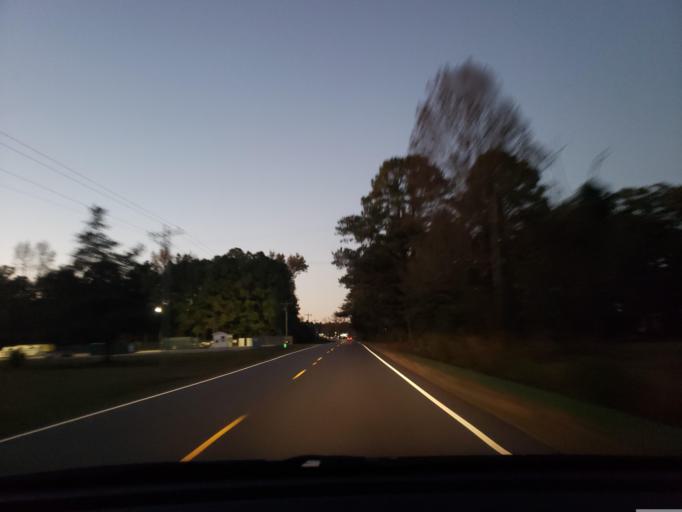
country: US
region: North Carolina
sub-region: Duplin County
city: Kenansville
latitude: 34.9360
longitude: -77.9419
